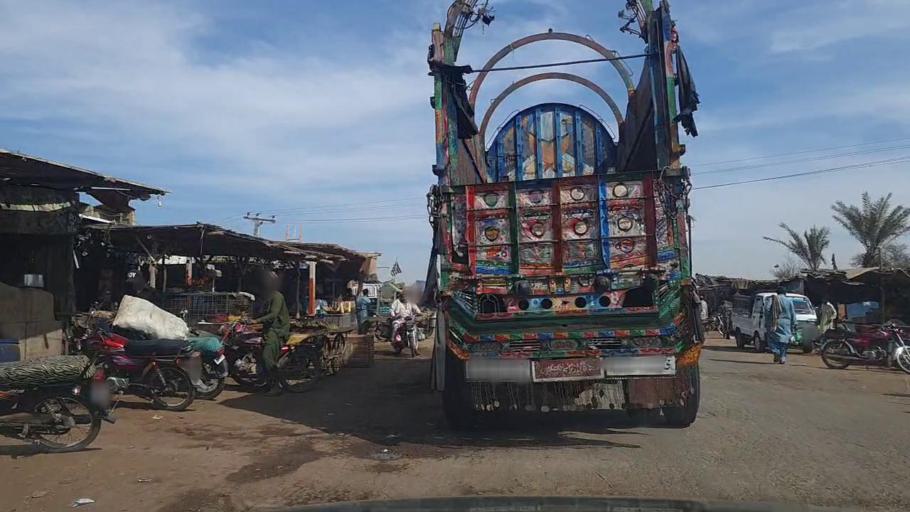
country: PK
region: Sindh
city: Daro Mehar
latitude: 24.9827
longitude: 68.1336
